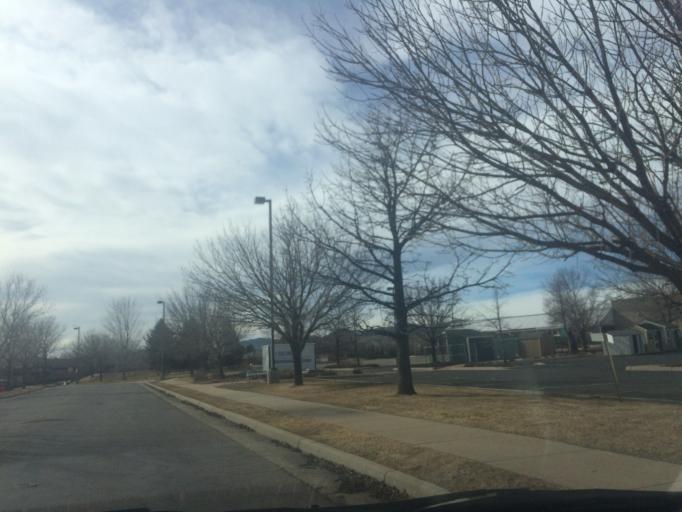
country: US
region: Colorado
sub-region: Boulder County
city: Superior
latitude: 39.9629
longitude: -105.1652
